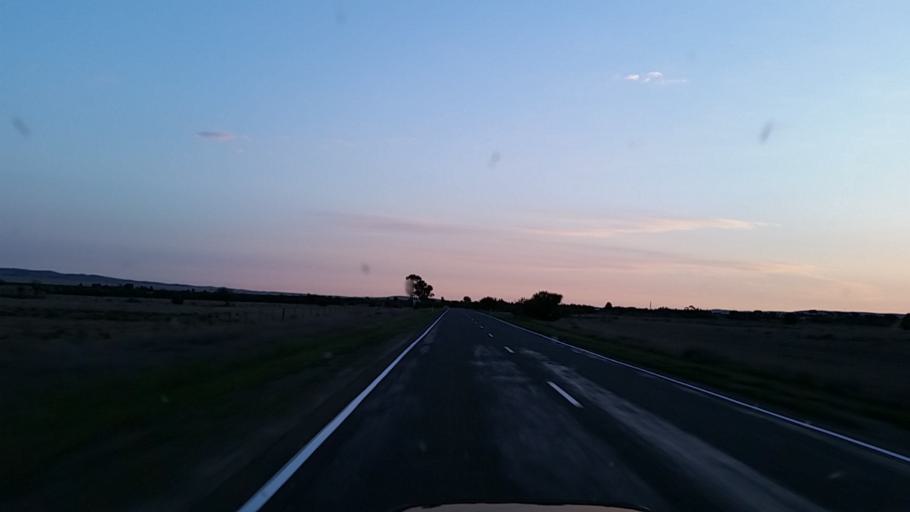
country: AU
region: South Australia
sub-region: Peterborough
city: Peterborough
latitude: -33.1430
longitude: 138.9294
